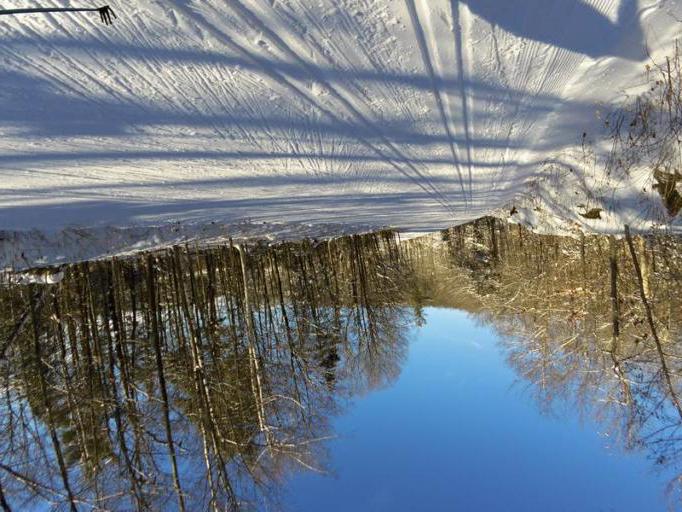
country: CA
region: Quebec
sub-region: Outaouais
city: Wakefield
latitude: 45.5093
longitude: -75.8790
